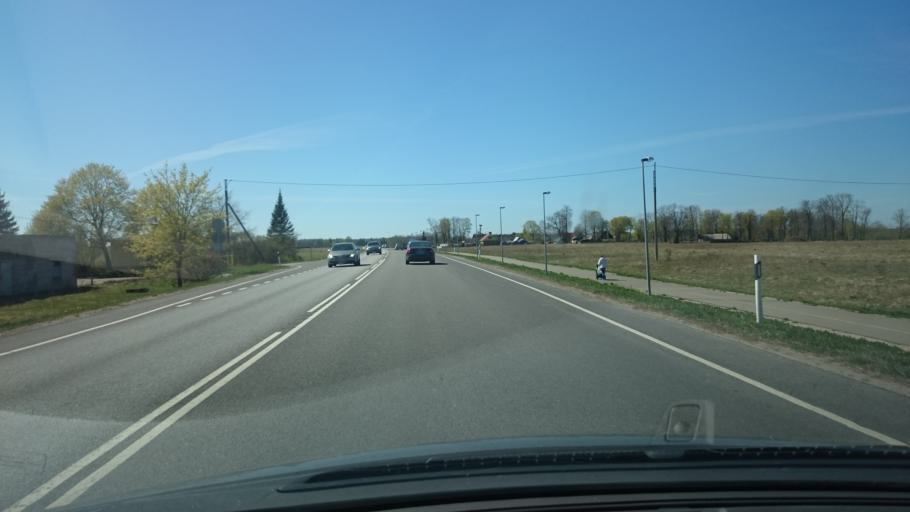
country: EE
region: Ida-Virumaa
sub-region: Narva linn
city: Narva
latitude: 59.3898
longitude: 28.1131
